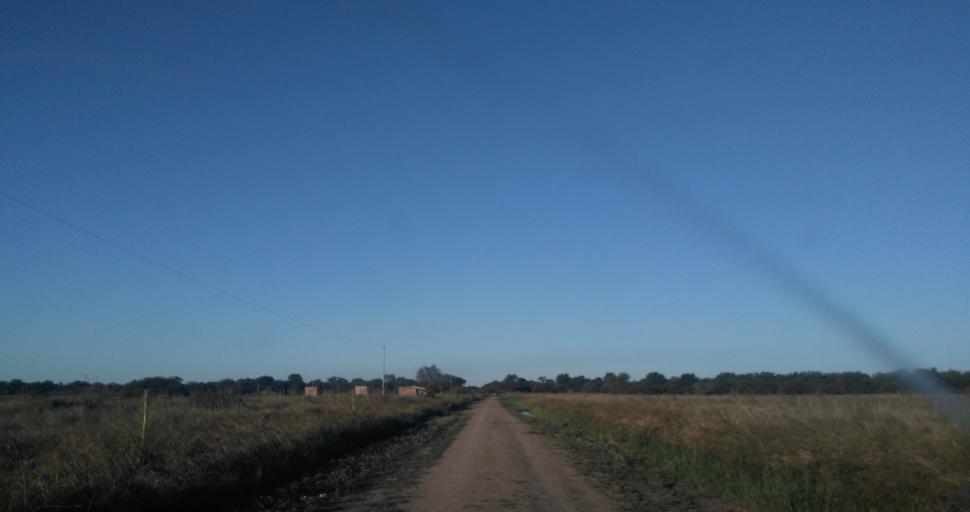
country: AR
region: Chaco
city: Fontana
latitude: -27.3884
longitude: -58.9757
